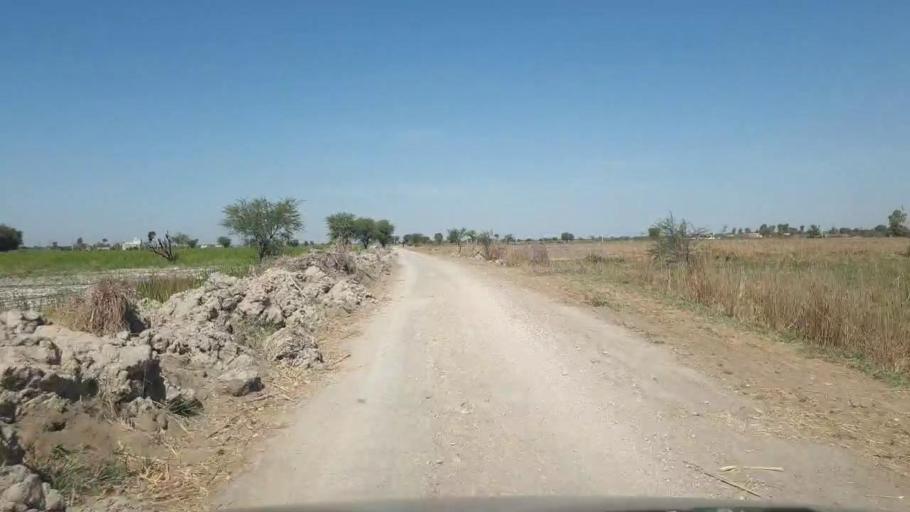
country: PK
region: Sindh
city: Dhoro Naro
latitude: 25.4423
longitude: 69.6169
